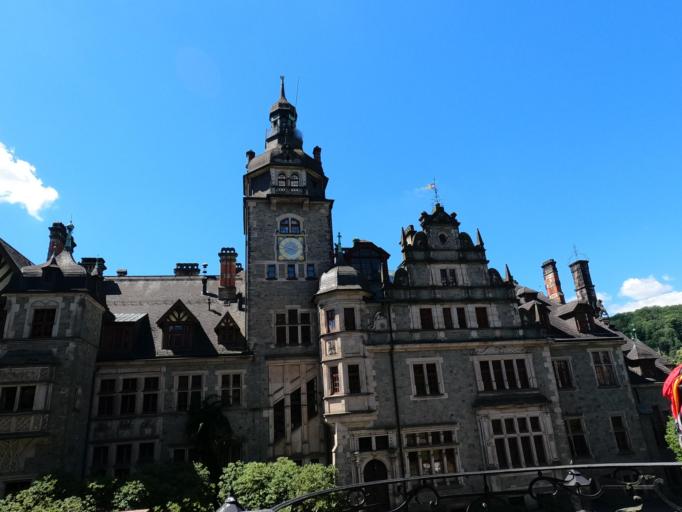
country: DE
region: Hesse
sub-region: Regierungsbezirk Darmstadt
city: Schluchtern
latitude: 50.3327
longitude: 9.6128
